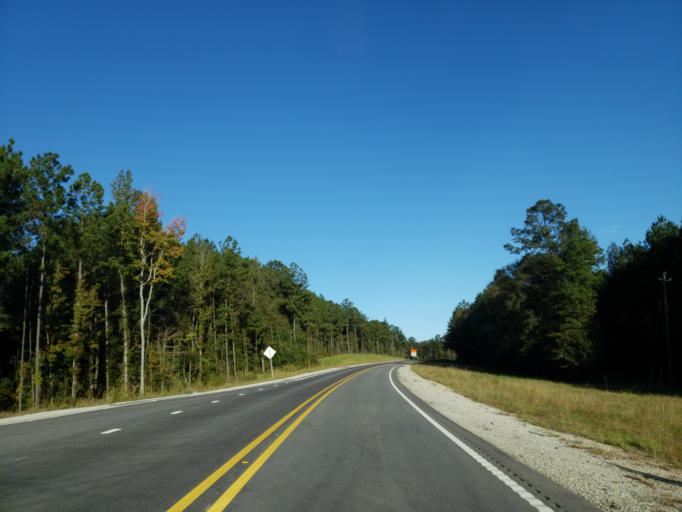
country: US
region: Mississippi
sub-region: Perry County
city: Richton
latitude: 31.3745
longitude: -88.8369
